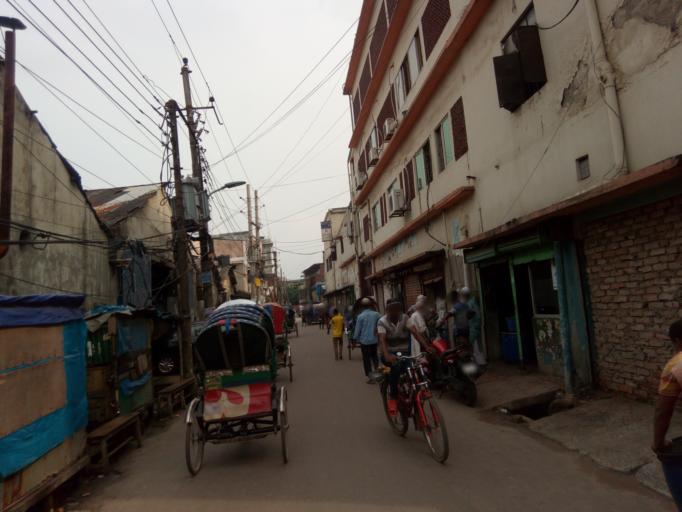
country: BD
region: Dhaka
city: Azimpur
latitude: 23.7361
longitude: 90.3682
